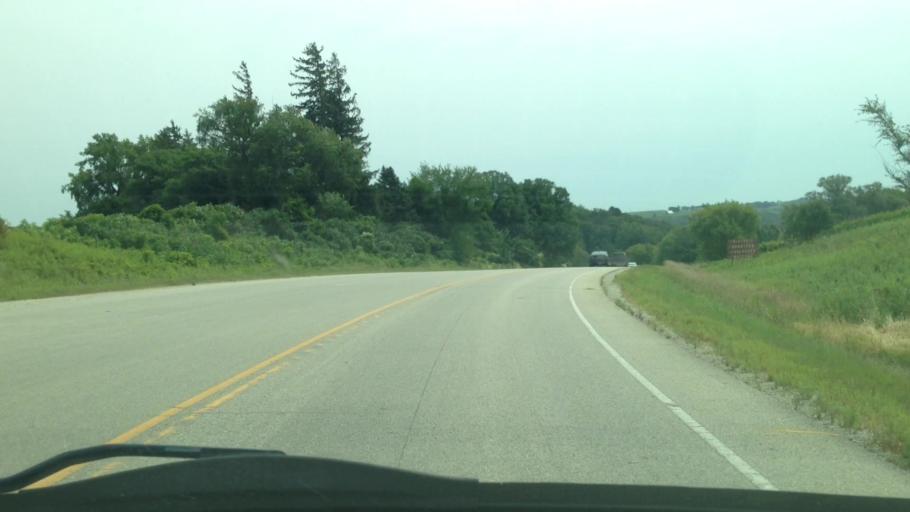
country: US
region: Minnesota
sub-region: Fillmore County
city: Preston
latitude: 43.7282
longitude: -91.9847
